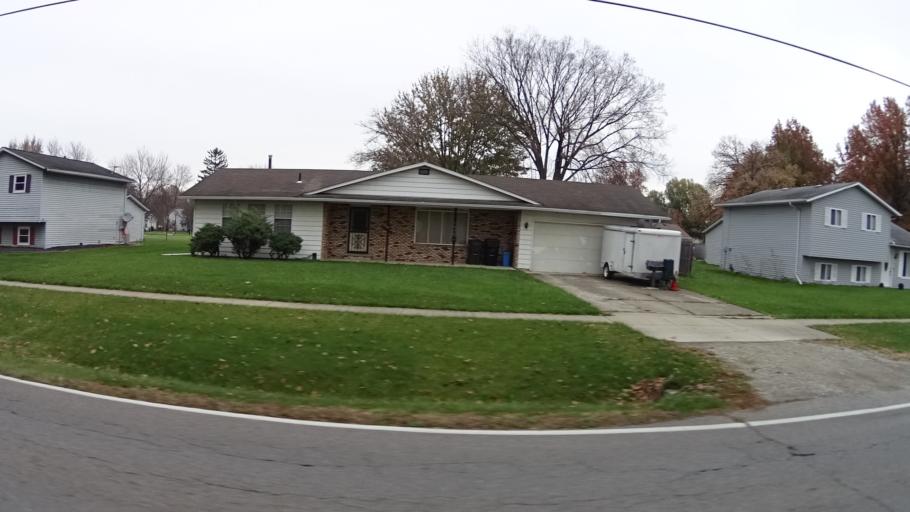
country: US
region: Ohio
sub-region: Lorain County
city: Elyria
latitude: 41.3430
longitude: -82.1076
